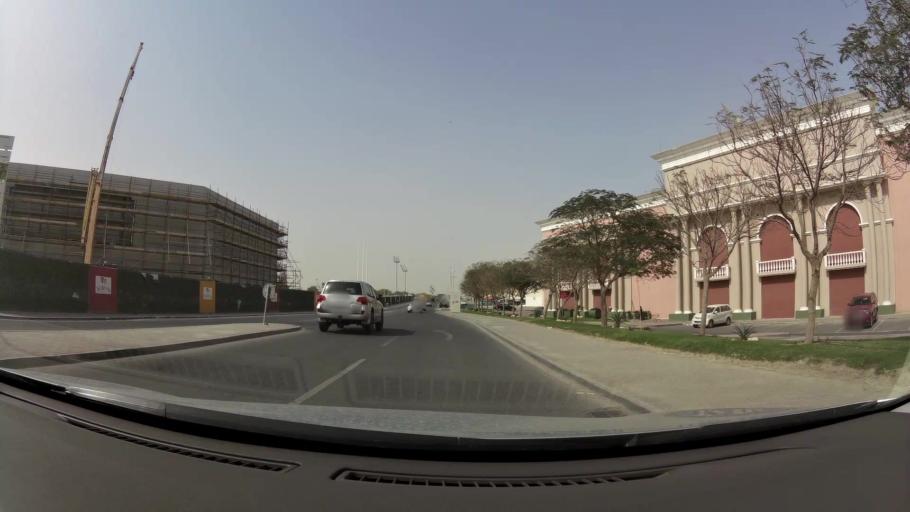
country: QA
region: Baladiyat ar Rayyan
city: Ar Rayyan
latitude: 25.2579
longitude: 51.4403
